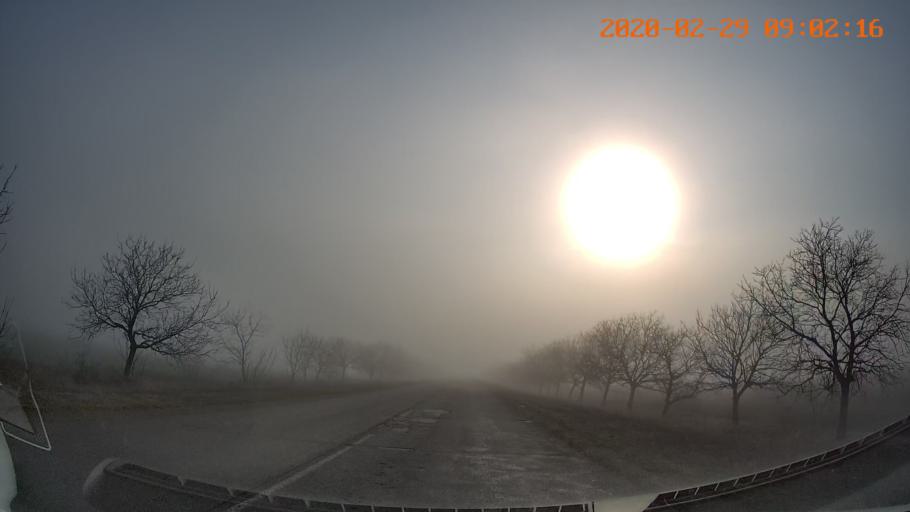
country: UA
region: Odessa
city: Velykoploske
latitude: 46.9215
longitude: 29.7074
